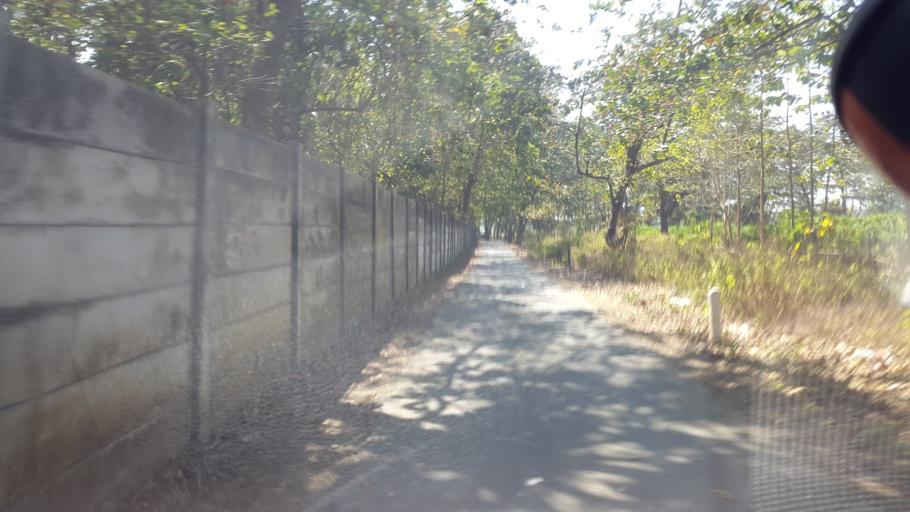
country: ID
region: West Java
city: Gunungbatu
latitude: -7.3307
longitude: 106.3987
